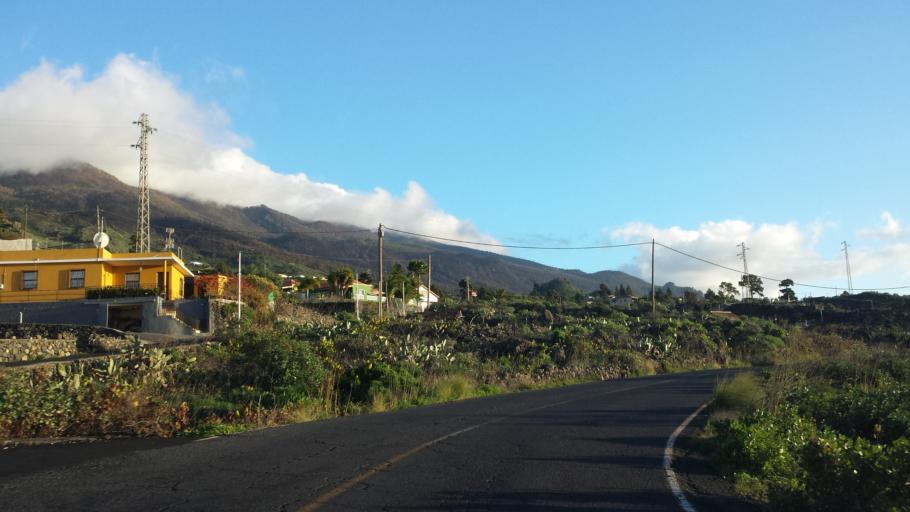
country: ES
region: Canary Islands
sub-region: Provincia de Santa Cruz de Tenerife
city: El Paso
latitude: 28.6252
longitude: -17.8848
